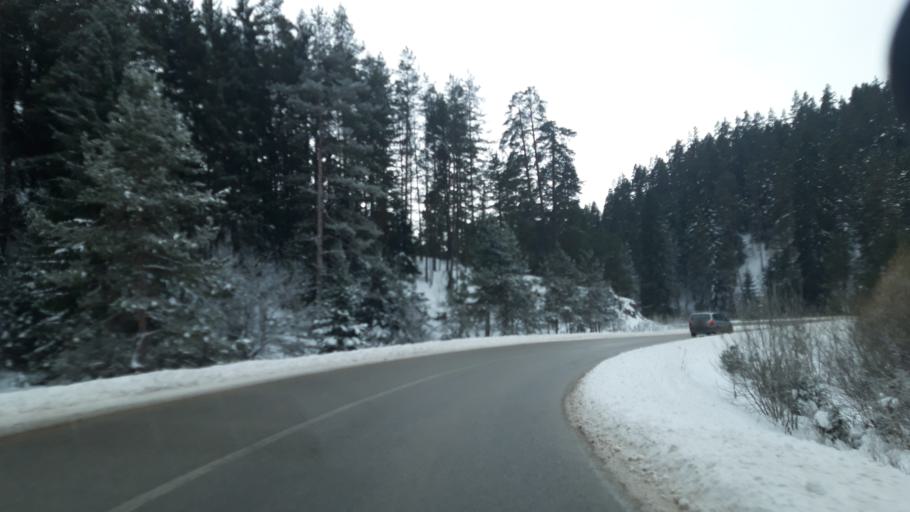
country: BA
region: Republika Srpska
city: Sokolac
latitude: 43.9825
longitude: 18.8621
